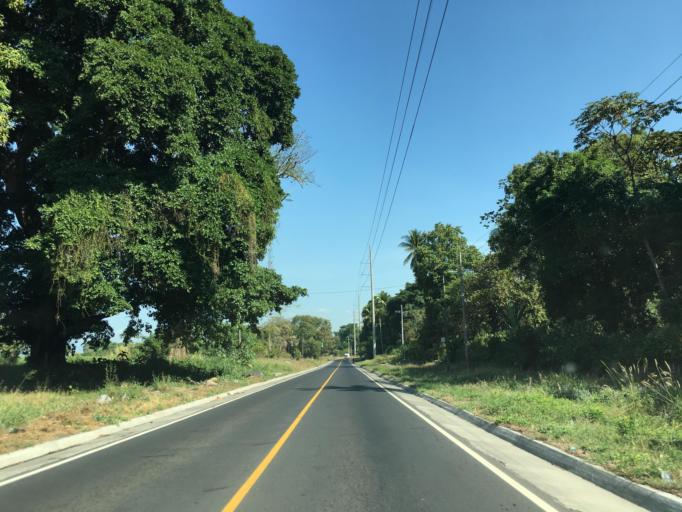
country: GT
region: Escuintla
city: Siquinala
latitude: 14.2842
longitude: -90.9689
